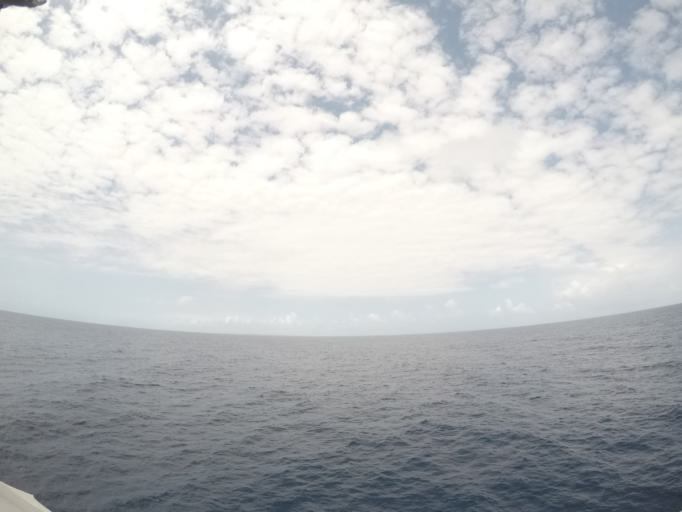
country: TZ
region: Zanzibar North
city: Nungwi
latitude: -5.6015
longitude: 39.3408
